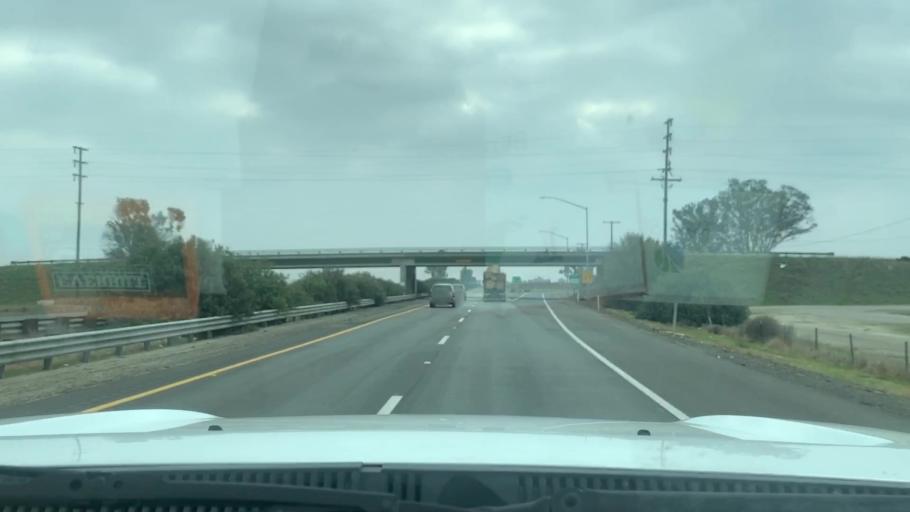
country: US
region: California
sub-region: Tulare County
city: Tipton
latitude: 36.1244
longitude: -119.3250
